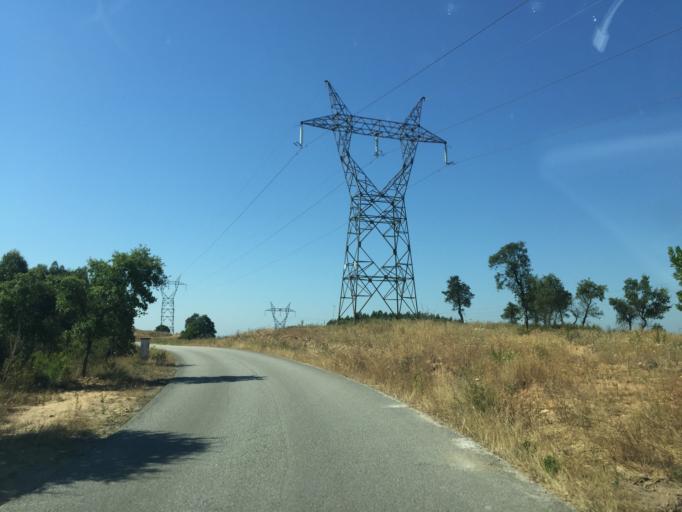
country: PT
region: Santarem
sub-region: Tomar
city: Tomar
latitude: 39.5661
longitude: -8.3208
